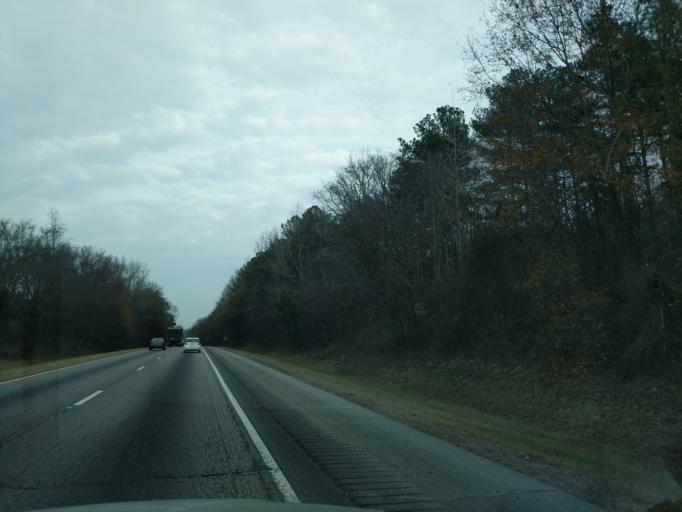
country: US
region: Georgia
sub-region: Jackson County
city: Braselton
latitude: 34.1343
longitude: -83.6762
